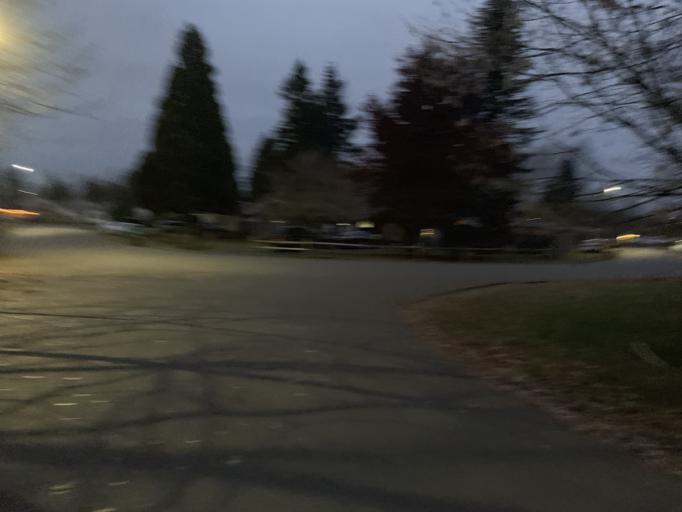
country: US
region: Washington
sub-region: Snohomish County
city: Marysville
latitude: 48.0879
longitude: -122.1650
